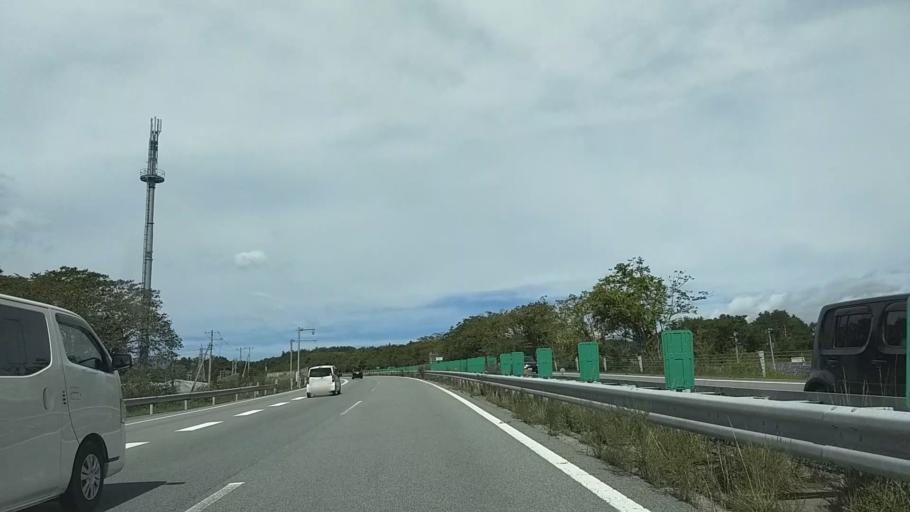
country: JP
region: Yamanashi
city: Nirasaki
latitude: 35.8524
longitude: 138.3422
